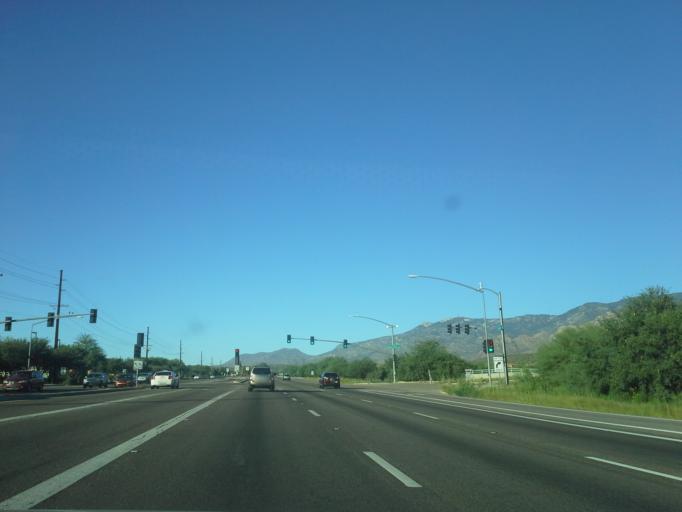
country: US
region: Arizona
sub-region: Pima County
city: Oro Valley
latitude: 32.3955
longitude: -110.9600
